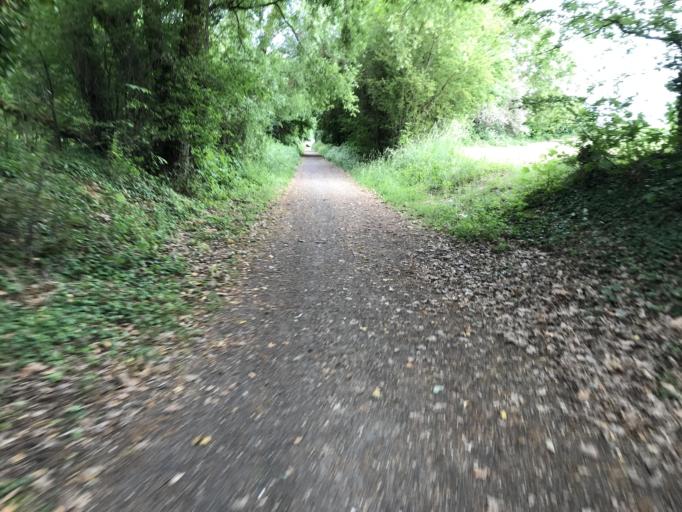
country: FR
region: Ile-de-France
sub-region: Departement de l'Essonne
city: Saulx-les-Chartreux
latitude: 48.6775
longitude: 2.2769
